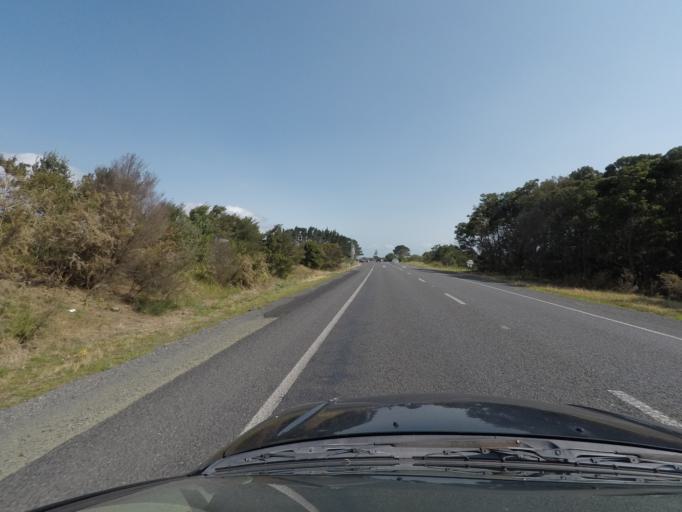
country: NZ
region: Northland
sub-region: Whangarei
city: Ruakaka
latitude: -35.9378
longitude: 174.4559
